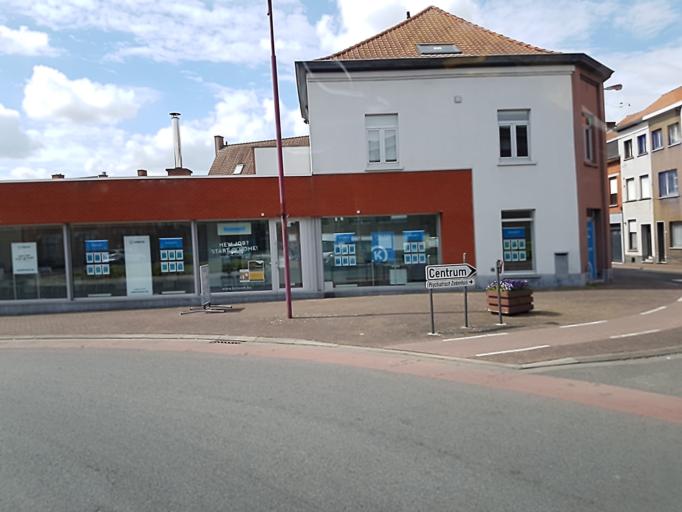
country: BE
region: Flanders
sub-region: Provincie West-Vlaanderen
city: Menen
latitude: 50.7968
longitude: 3.1264
